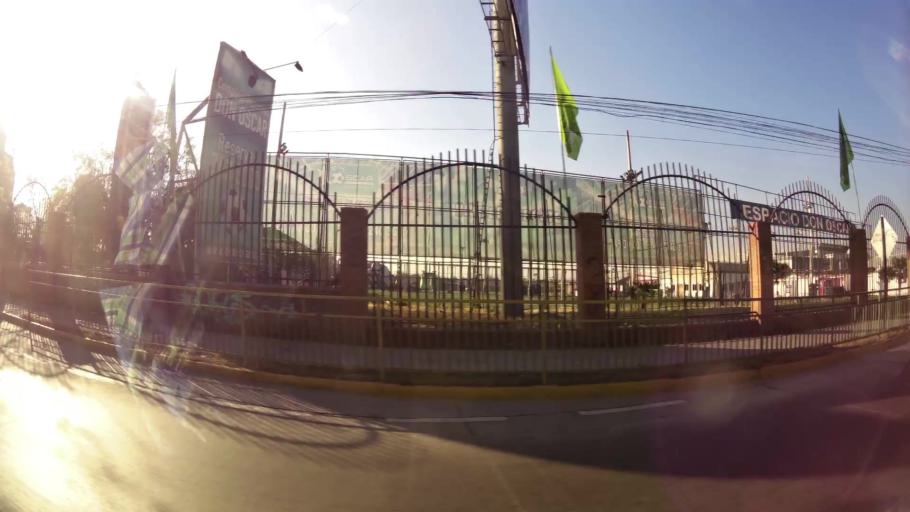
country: CL
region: Santiago Metropolitan
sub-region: Provincia de Santiago
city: Lo Prado
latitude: -33.4848
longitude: -70.7467
